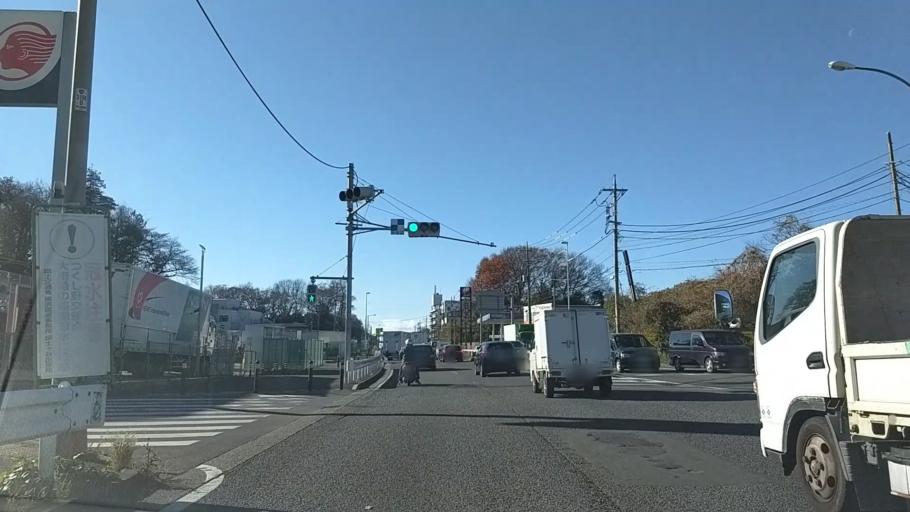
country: JP
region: Tokyo
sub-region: Machida-shi
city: Machida
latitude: 35.5194
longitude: 139.4845
